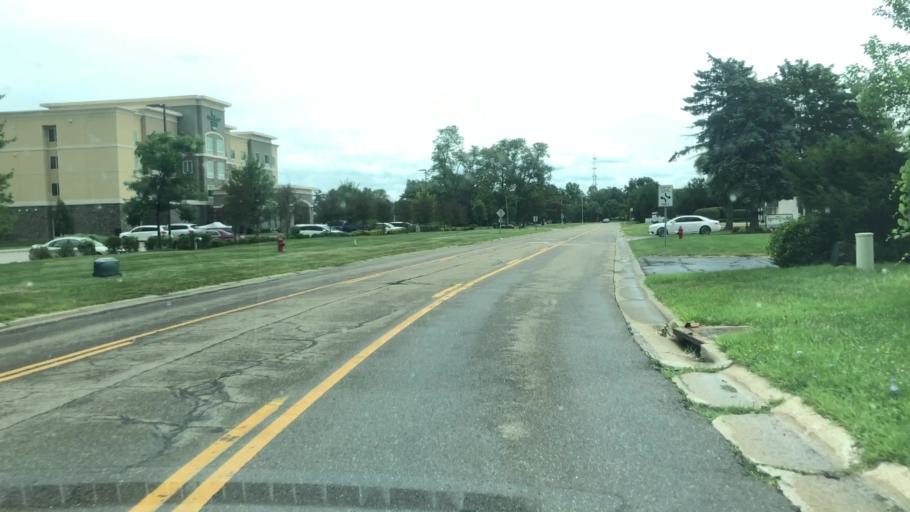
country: US
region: Ohio
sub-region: Summit County
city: Montrose-Ghent
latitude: 41.1402
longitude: -81.6460
